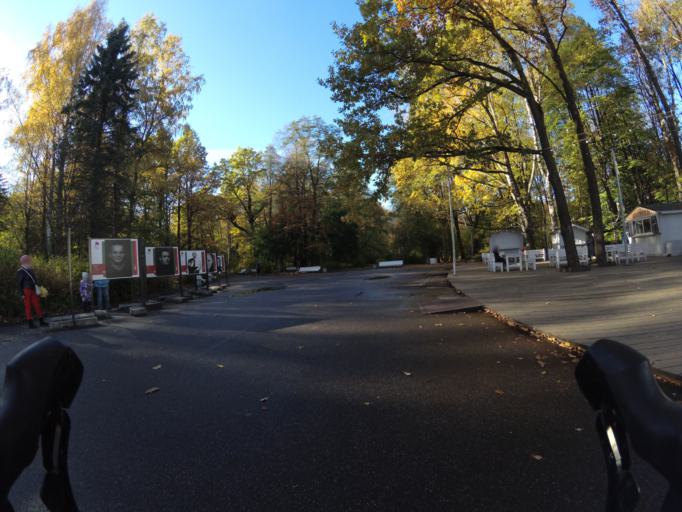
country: RU
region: Leningrad
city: Krestovskiy ostrov
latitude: 59.9796
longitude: 30.2646
